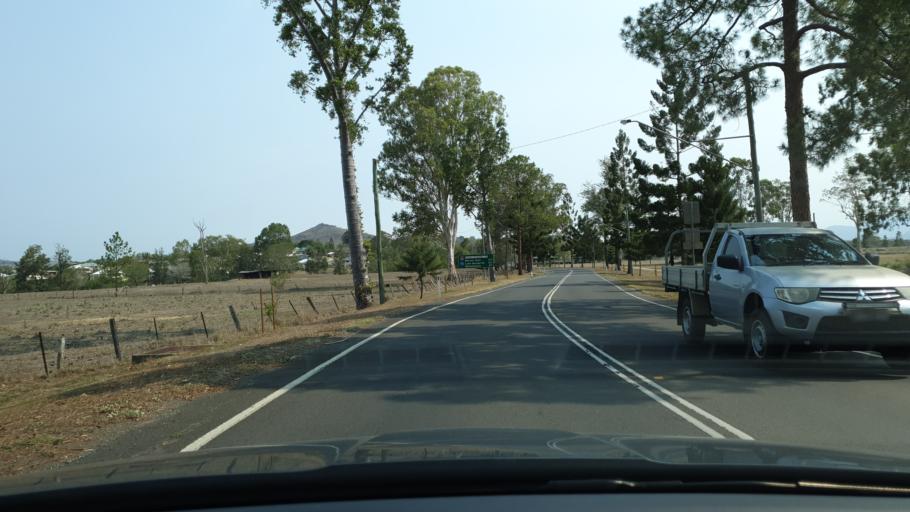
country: AU
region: Queensland
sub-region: Ipswich
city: Deebing Heights
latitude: -28.0011
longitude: 152.6819
